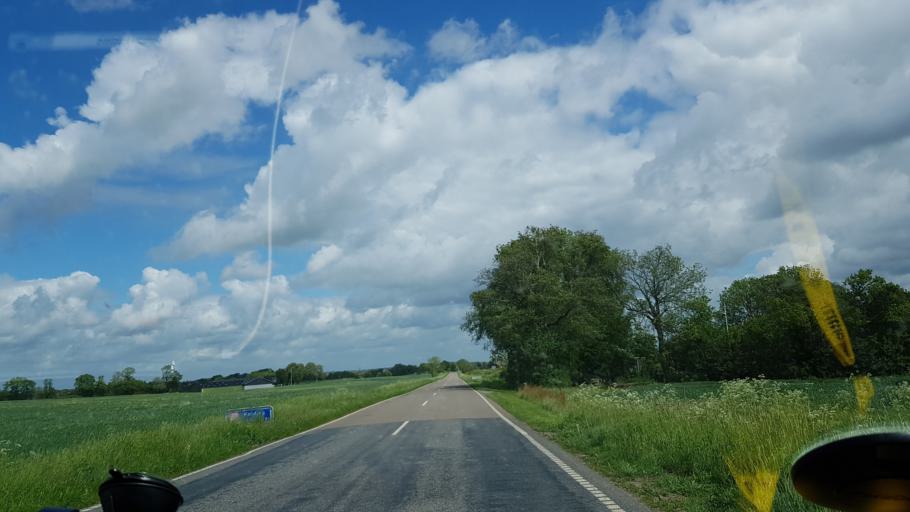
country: DK
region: South Denmark
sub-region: Kolding Kommune
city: Christiansfeld
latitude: 55.3343
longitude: 9.4520
